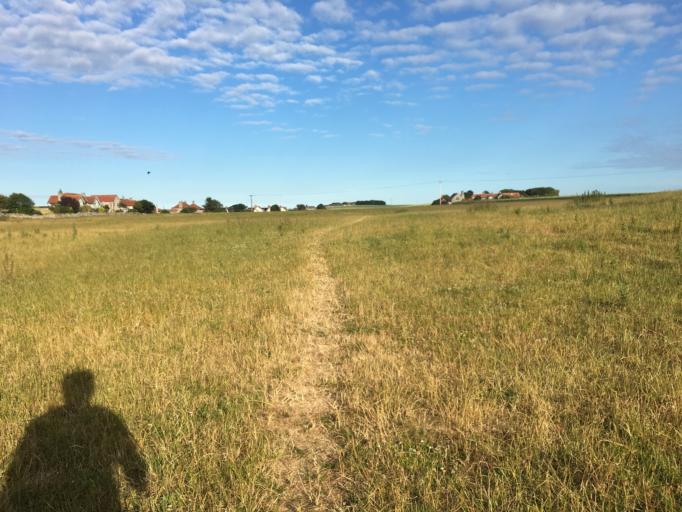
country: GB
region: England
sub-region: Northumberland
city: Bamburgh
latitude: 55.6054
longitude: -1.7057
